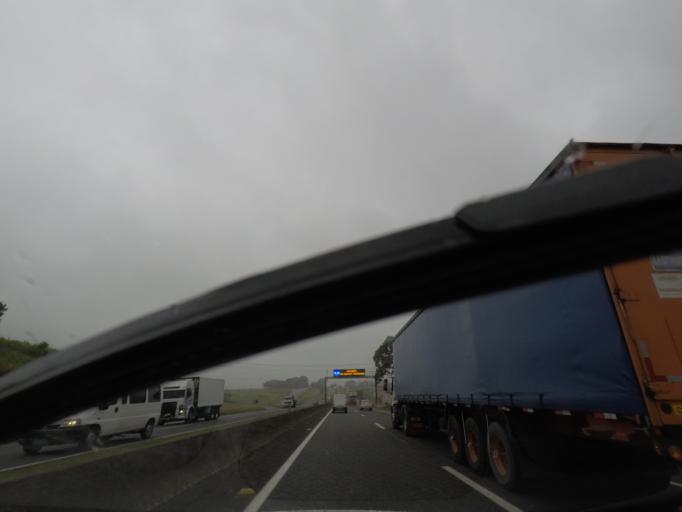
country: BR
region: Sao Paulo
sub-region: Taubate
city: Taubate
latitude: -23.0554
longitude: -45.6121
